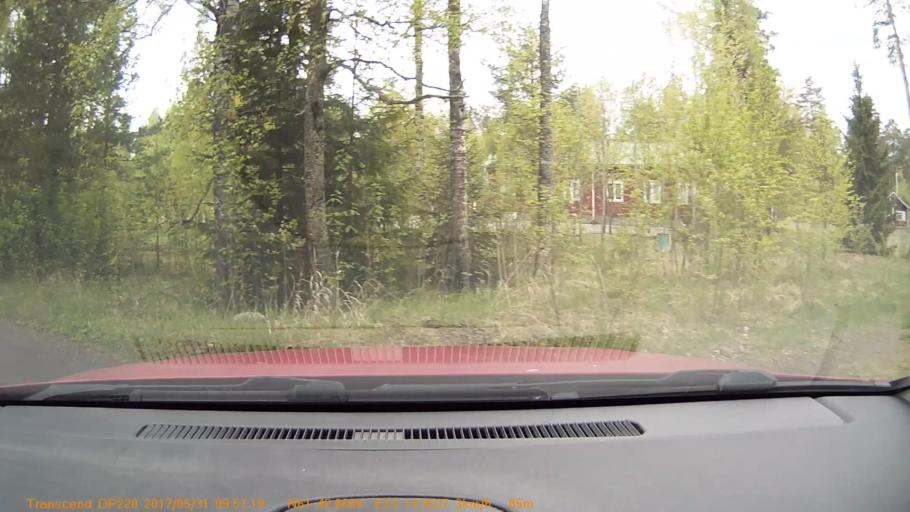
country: FI
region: Pirkanmaa
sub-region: Tampere
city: Viljakkala
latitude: 61.7111
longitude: 23.2392
